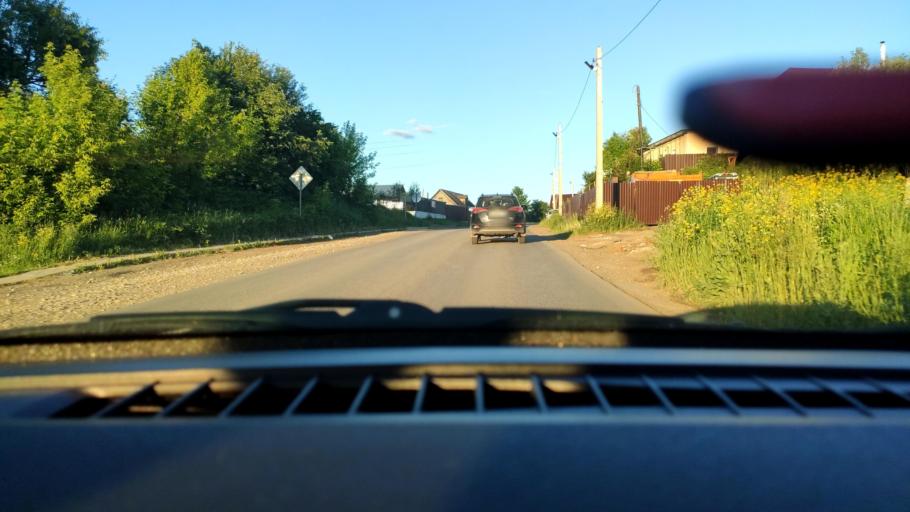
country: RU
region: Perm
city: Kultayevo
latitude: 57.9289
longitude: 56.0069
